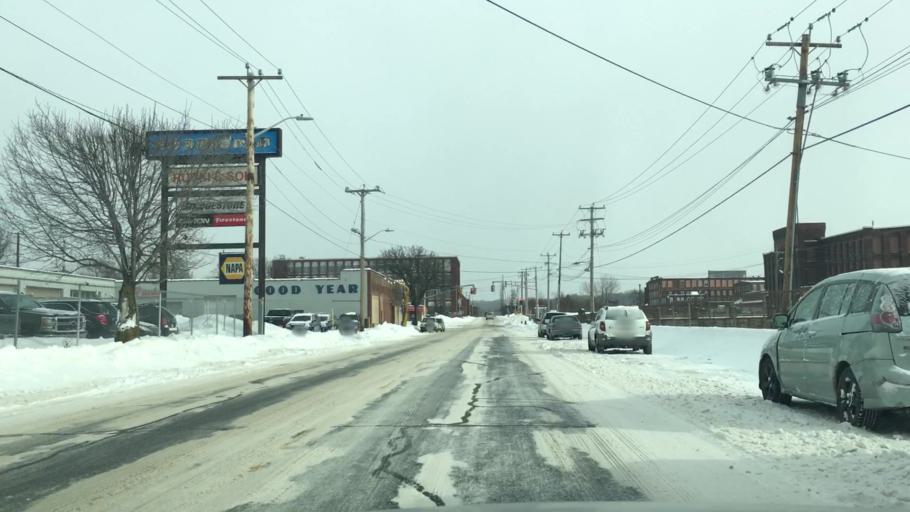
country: US
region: Massachusetts
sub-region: Hampden County
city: North Chicopee
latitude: 42.1963
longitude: -72.6046
